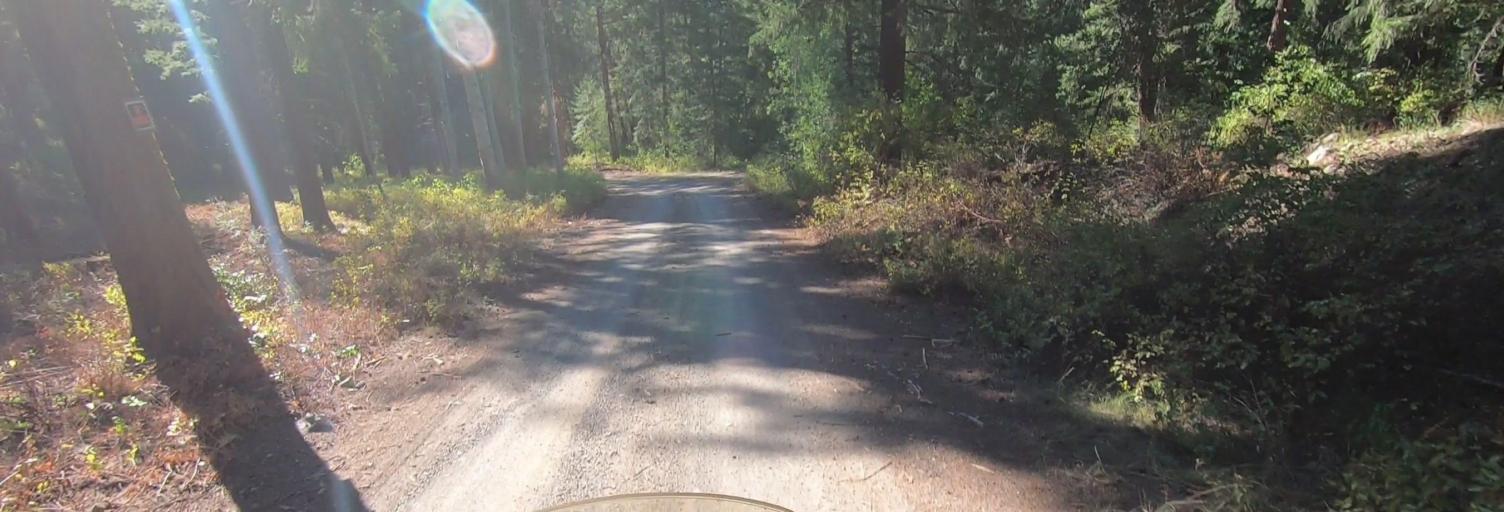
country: US
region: Washington
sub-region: Chelan County
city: Granite Falls
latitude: 48.5237
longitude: -120.3118
